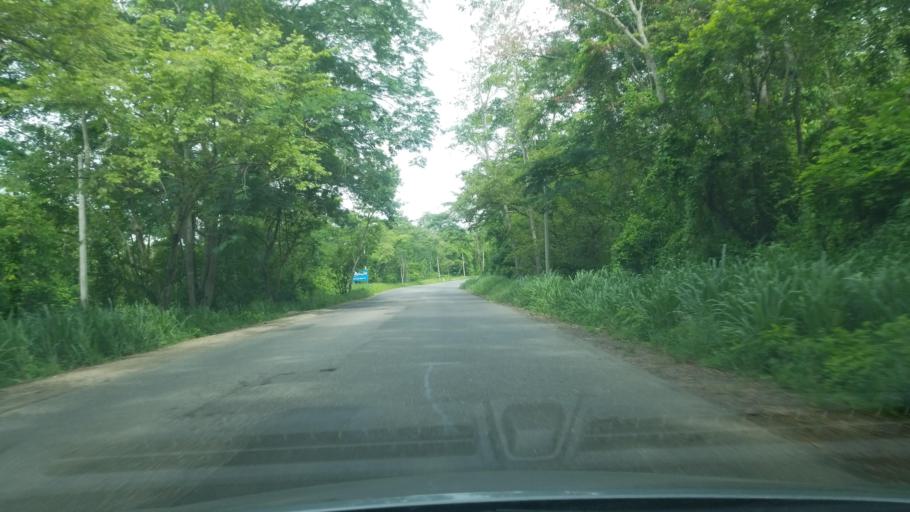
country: HN
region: Santa Barbara
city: Camalote
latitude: 15.3309
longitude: -88.3396
